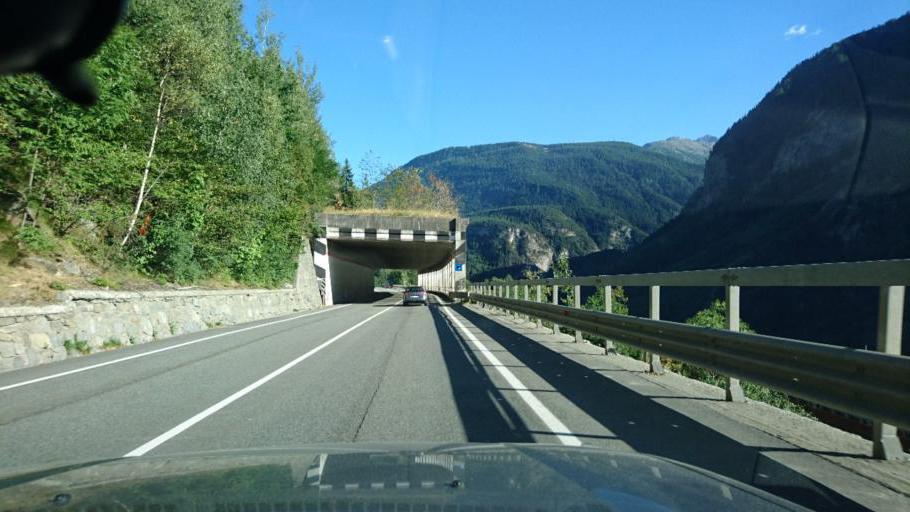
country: IT
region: Aosta Valley
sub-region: Valle d'Aosta
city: Courmayeur
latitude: 45.7789
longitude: 6.9740
